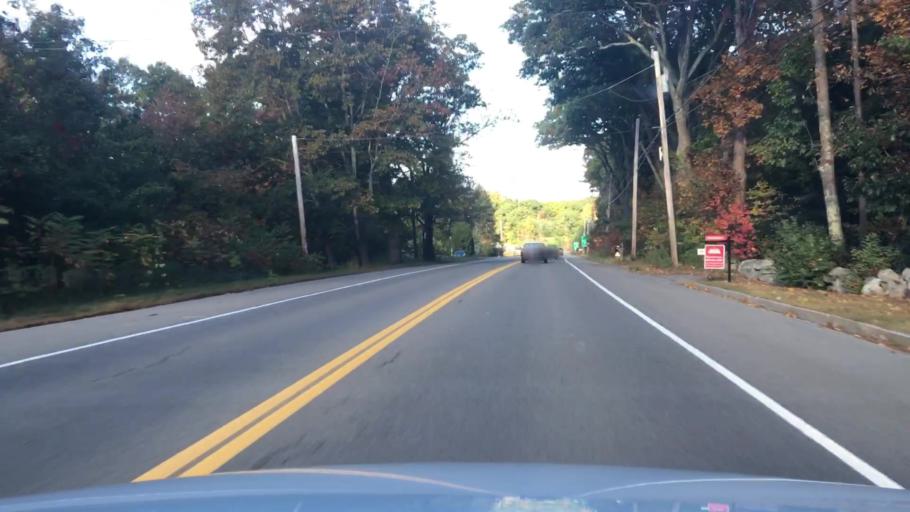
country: US
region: New Hampshire
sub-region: Strafford County
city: Durham
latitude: 43.1367
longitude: -70.8959
